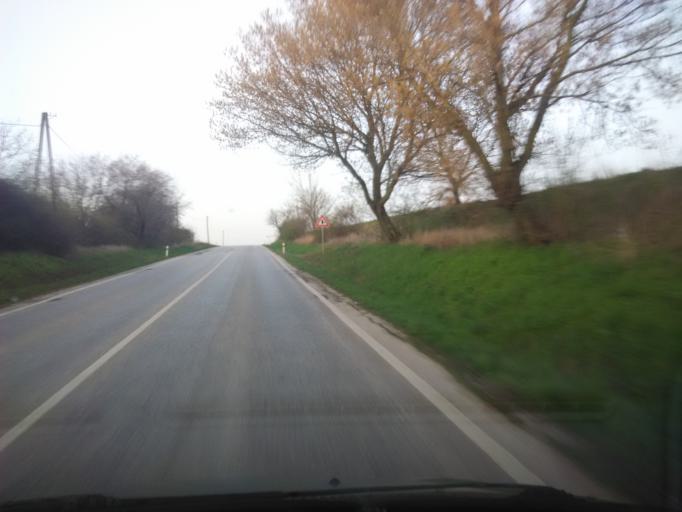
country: SK
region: Nitriansky
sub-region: Okres Nitra
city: Nitra
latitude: 48.2378
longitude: 18.0102
